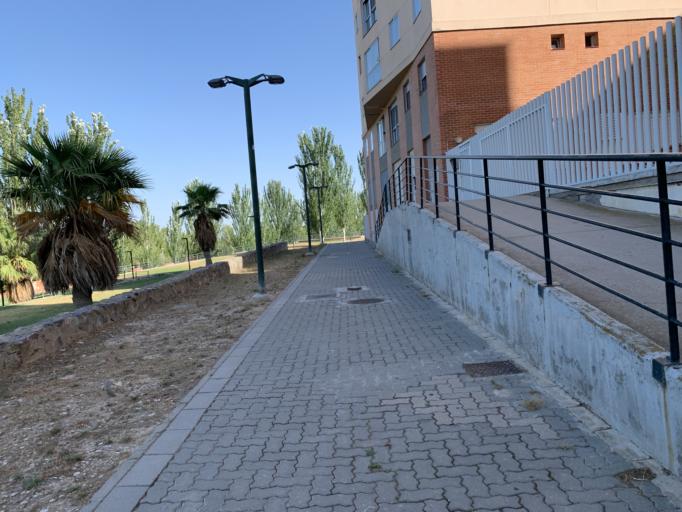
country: ES
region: Aragon
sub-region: Provincia de Zaragoza
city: Zaragoza
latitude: 41.6279
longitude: -0.8729
